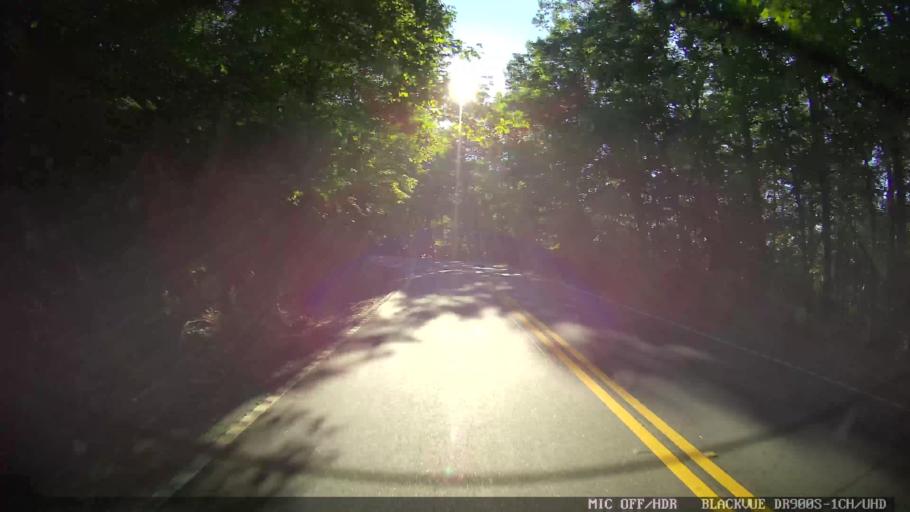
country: US
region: Georgia
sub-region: Lumpkin County
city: Dahlonega
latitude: 34.6261
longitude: -83.9561
